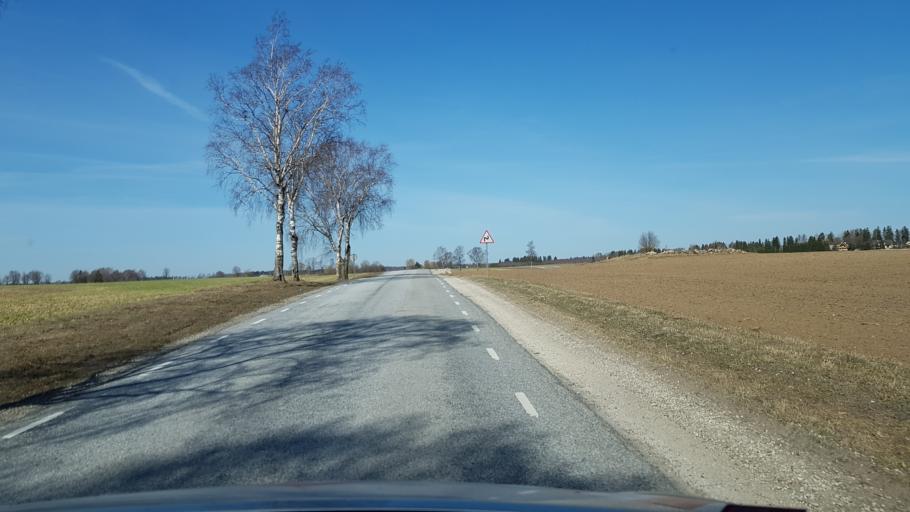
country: EE
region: Laeaene-Virumaa
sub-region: Vinni vald
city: Vinni
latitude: 59.2982
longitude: 26.4186
